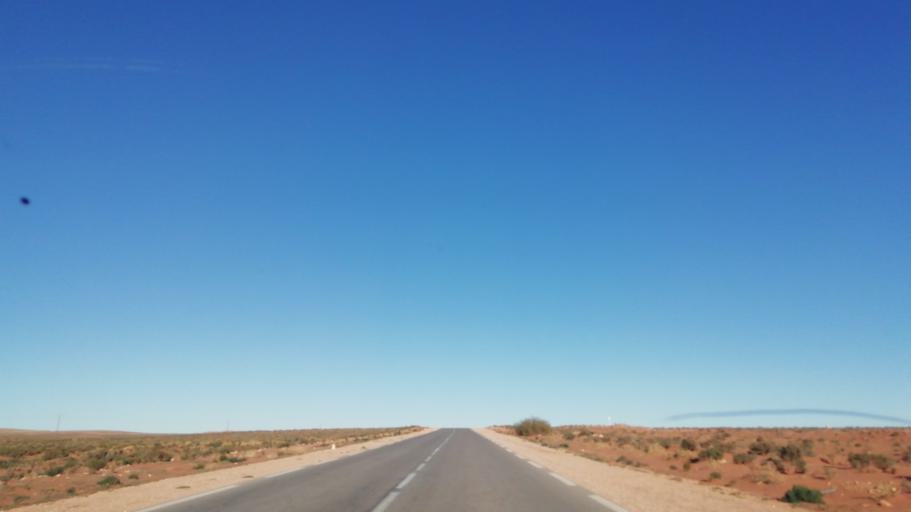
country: DZ
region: El Bayadh
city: El Abiodh Sidi Cheikh
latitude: 33.1234
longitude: 0.2782
